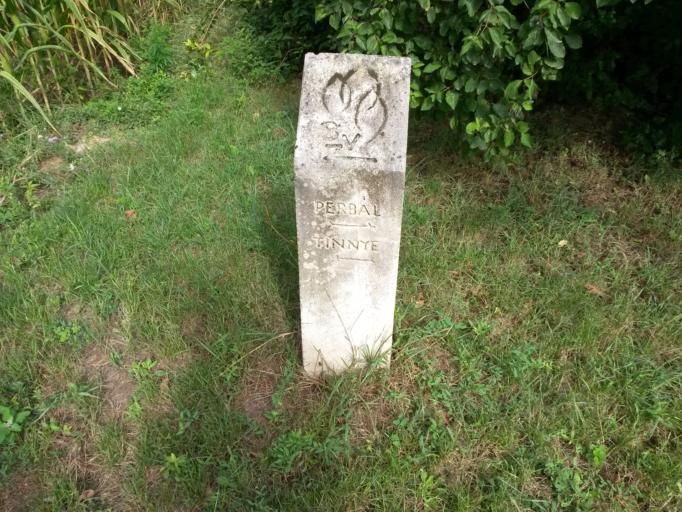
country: HU
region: Pest
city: Perbal
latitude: 47.5955
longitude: 18.7630
